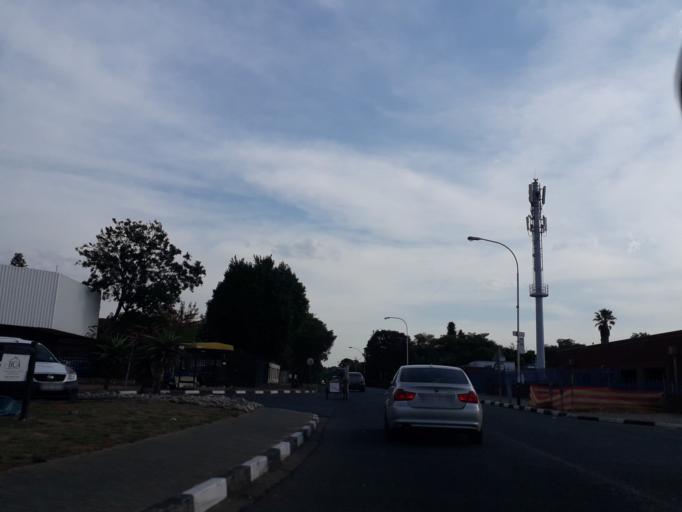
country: ZA
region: Gauteng
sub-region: City of Johannesburg Metropolitan Municipality
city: Johannesburg
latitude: -26.1164
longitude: 28.0011
